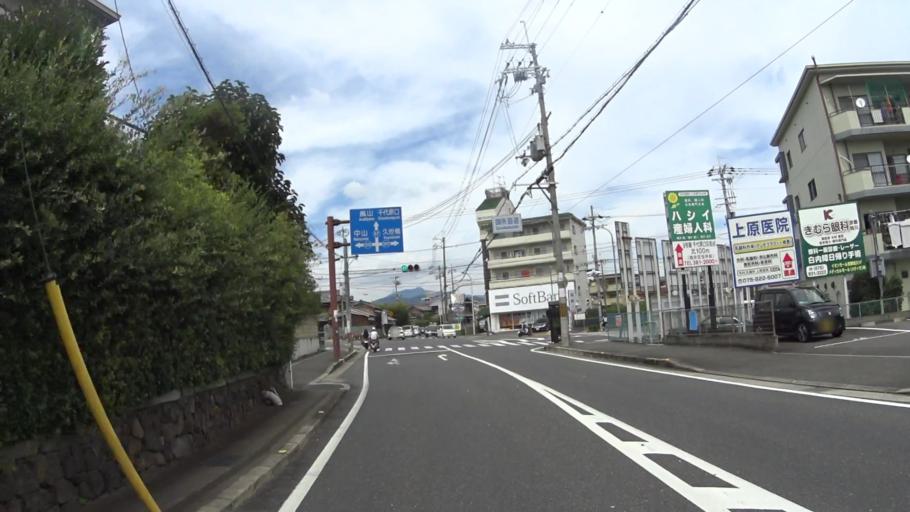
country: JP
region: Kyoto
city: Muko
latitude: 34.9638
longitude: 135.6960
